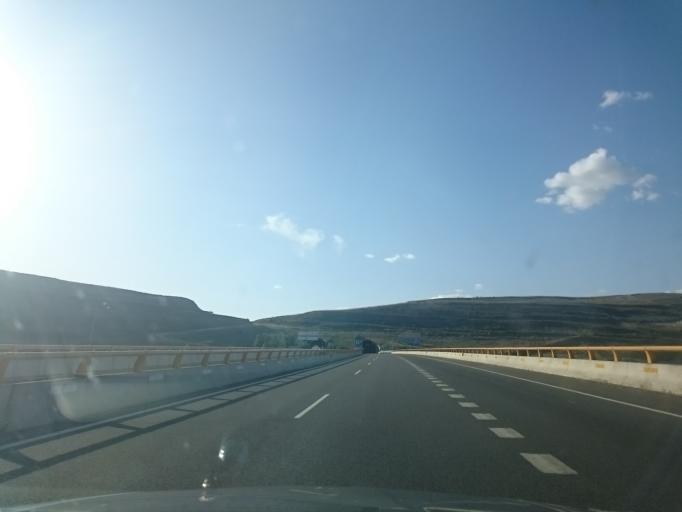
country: ES
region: Castille and Leon
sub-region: Provincia de Burgos
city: San Mames de Burgos
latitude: 42.3533
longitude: -3.7969
